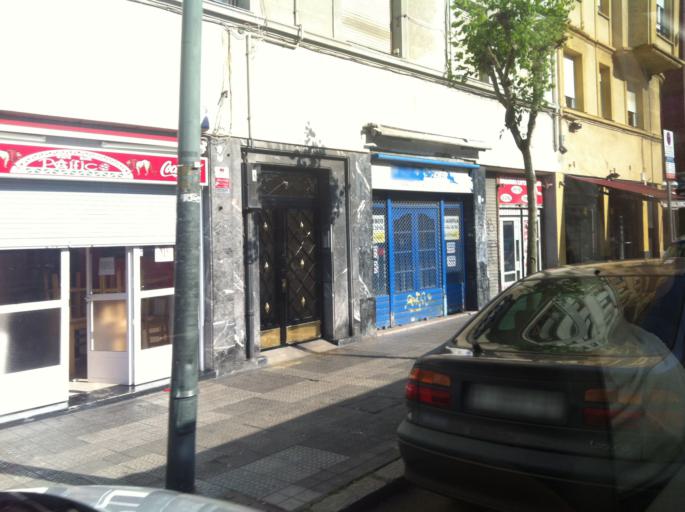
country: ES
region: Basque Country
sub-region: Bizkaia
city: Bilbao
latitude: 43.2637
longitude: -2.9469
